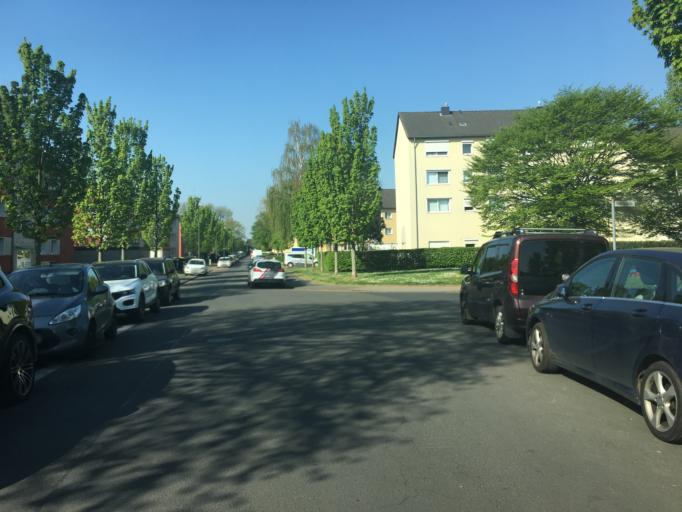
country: DE
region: North Rhine-Westphalia
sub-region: Regierungsbezirk Koln
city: Muelheim
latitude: 50.9950
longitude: 6.9918
